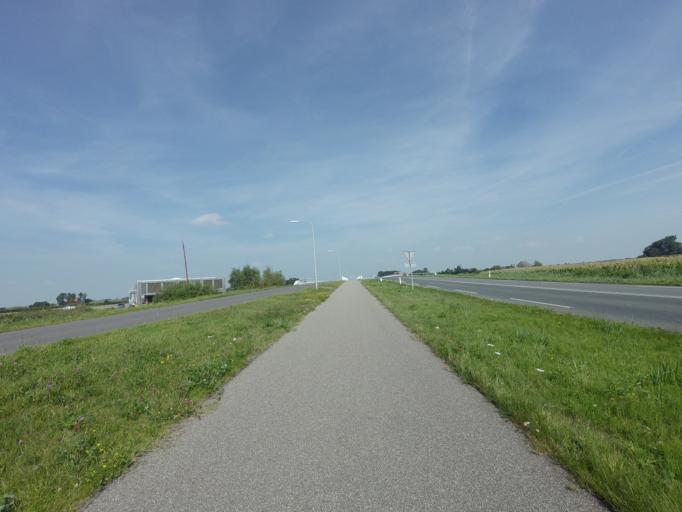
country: NL
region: Friesland
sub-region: Sudwest Fryslan
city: Woudsend
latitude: 52.9430
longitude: 5.6481
